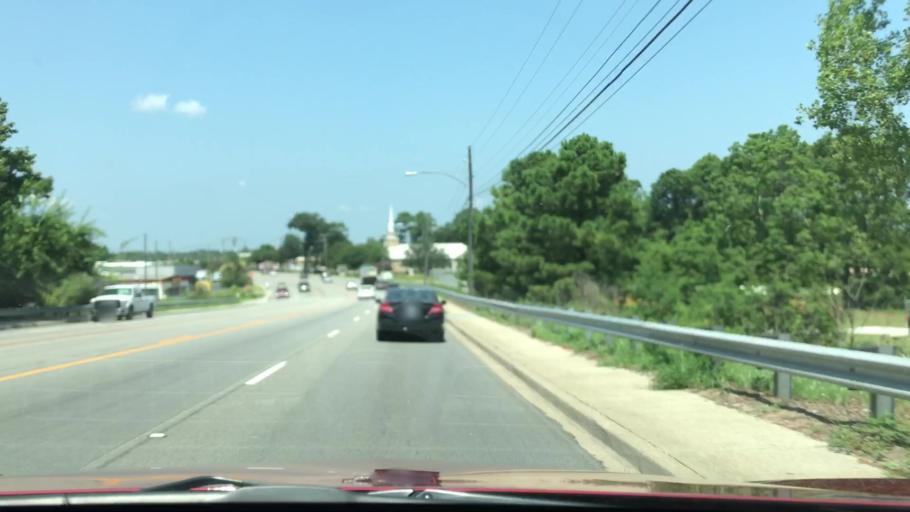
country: US
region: South Carolina
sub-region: Charleston County
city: North Charleston
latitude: 32.8568
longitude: -80.0268
